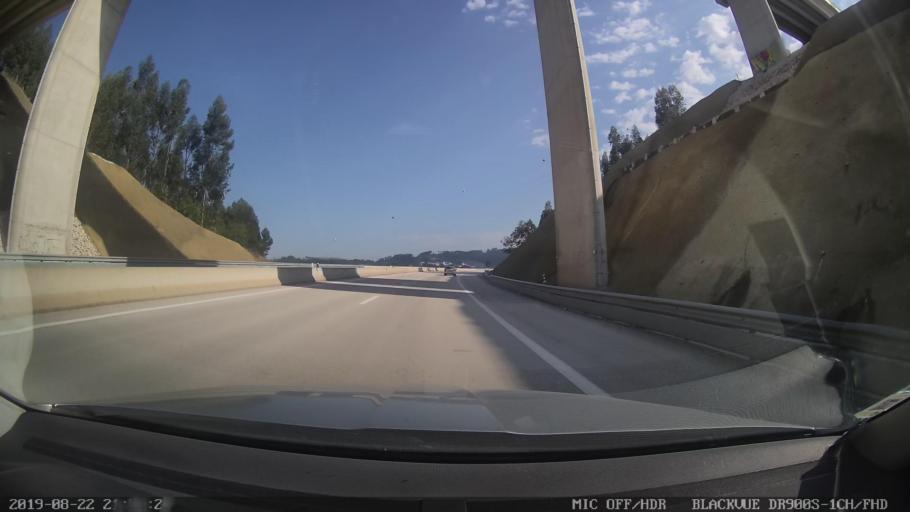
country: PT
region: Coimbra
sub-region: Coimbra
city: Coimbra
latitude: 40.1684
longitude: -8.3786
